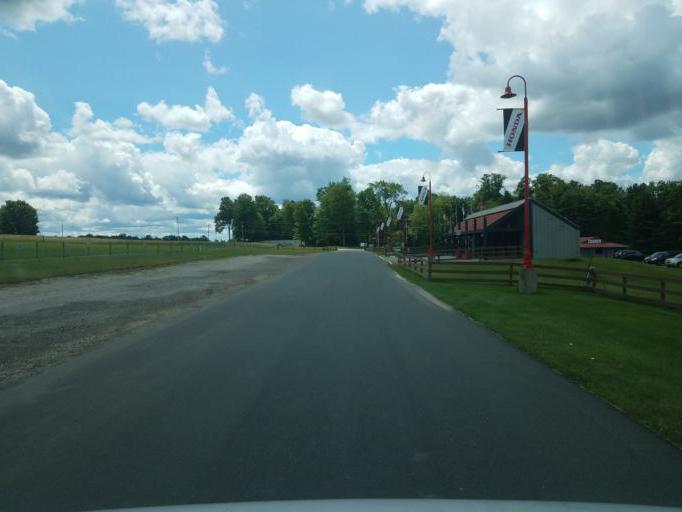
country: US
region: Ohio
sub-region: Richland County
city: Lexington
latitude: 40.6824
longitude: -82.6383
